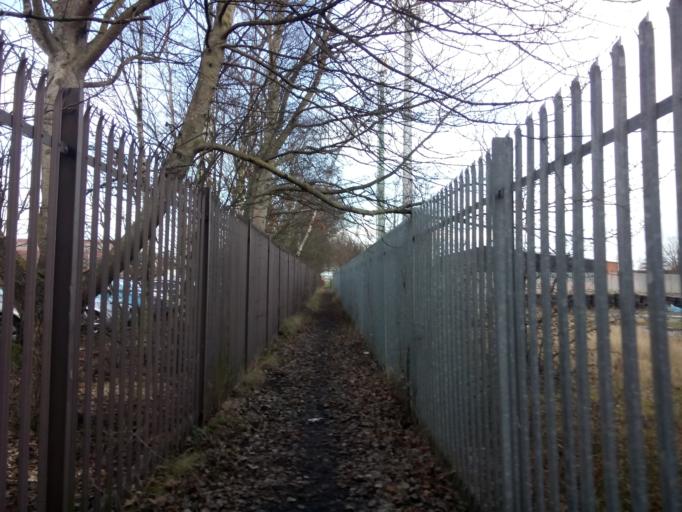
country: GB
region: England
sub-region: County Durham
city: Durham
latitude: 54.8033
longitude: -1.5813
